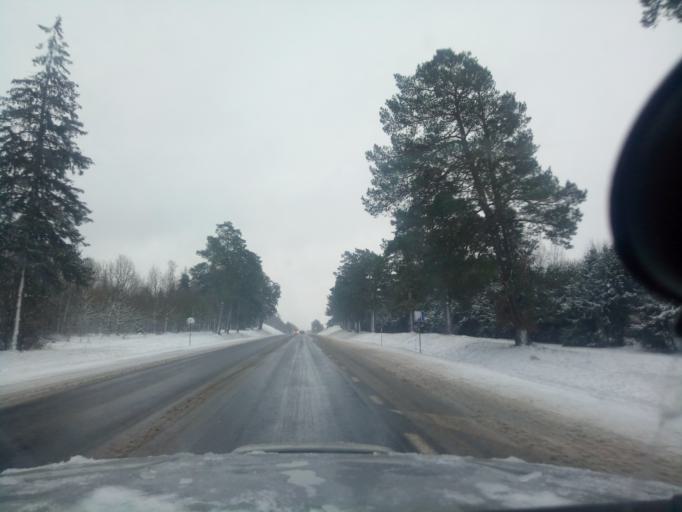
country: BY
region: Minsk
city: Haradzyeya
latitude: 53.2698
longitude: 26.6011
